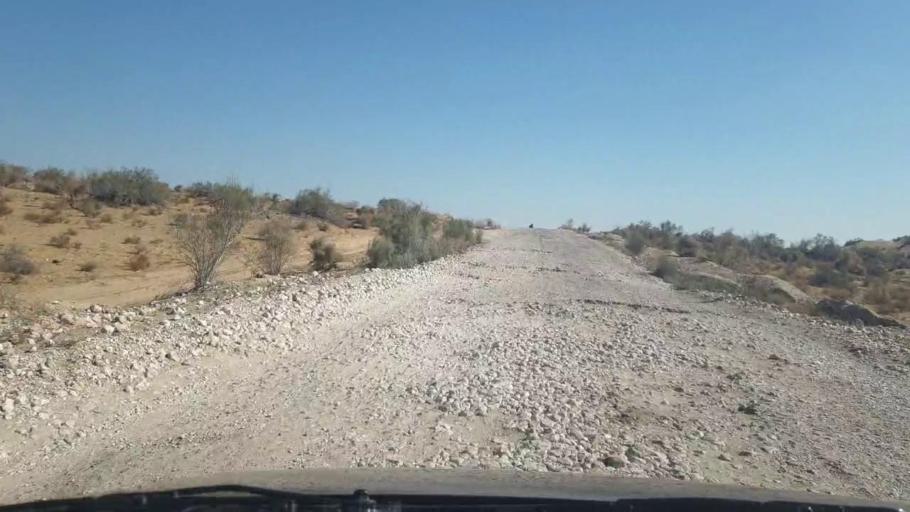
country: PK
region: Sindh
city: Bozdar
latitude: 26.9999
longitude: 68.8517
